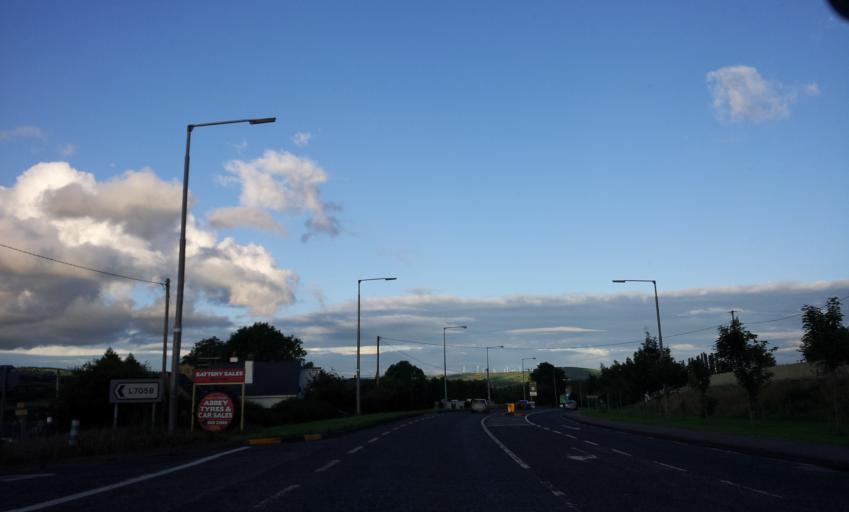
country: IE
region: Munster
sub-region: County Limerick
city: Abbeyfeale
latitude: 52.3888
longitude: -9.2841
